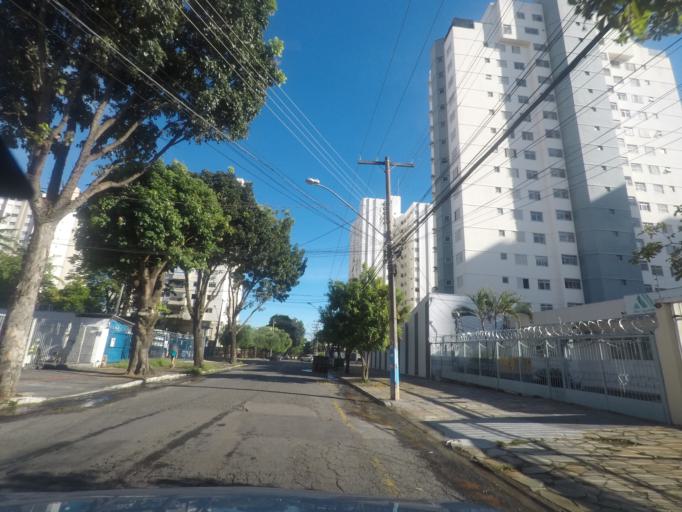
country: BR
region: Goias
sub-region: Goiania
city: Goiania
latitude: -16.6694
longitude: -49.2677
